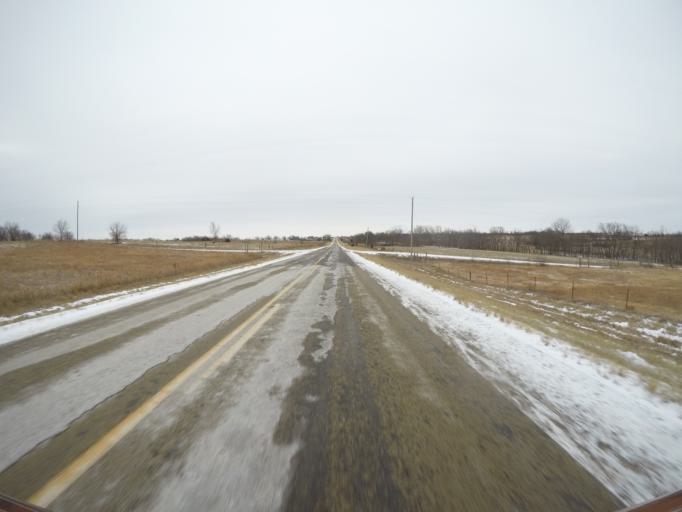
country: US
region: Kansas
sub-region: Pottawatomie County
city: Saint Marys
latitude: 39.1157
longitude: -96.1688
